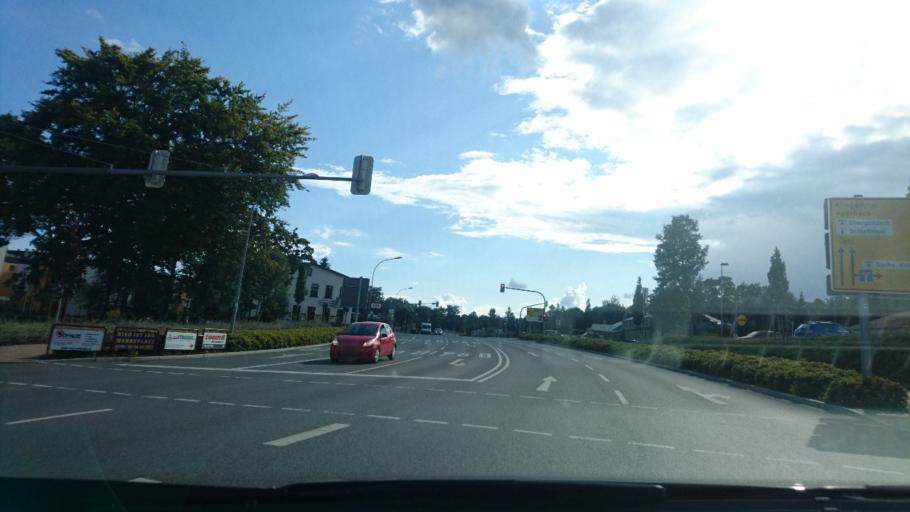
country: DE
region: Saxony
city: Rodewisch
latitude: 50.5323
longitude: 12.4035
